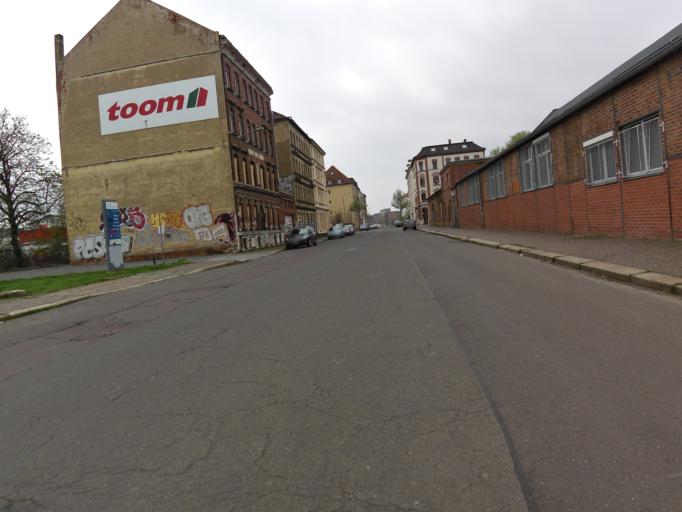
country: DE
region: Saxony
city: Leipzig
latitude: 51.3254
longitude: 12.3287
